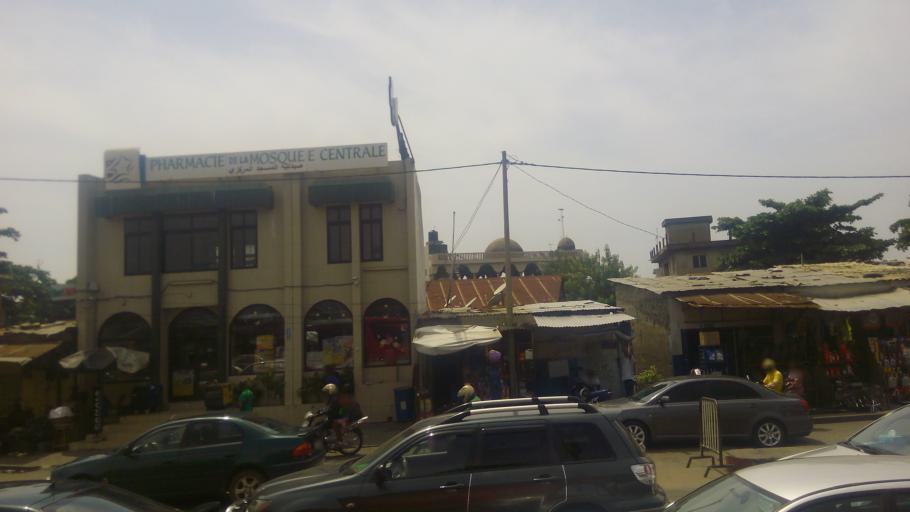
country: BJ
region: Littoral
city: Cotonou
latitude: 6.3575
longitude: 2.4260
